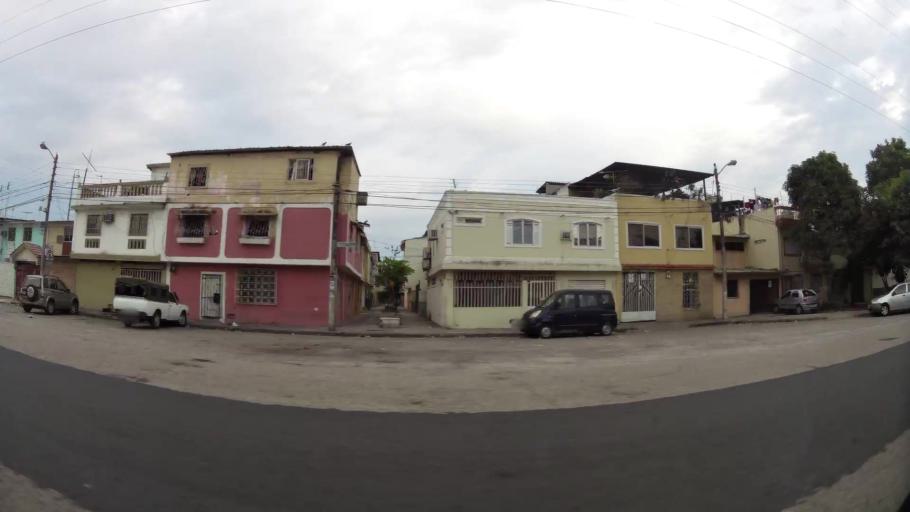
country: EC
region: Guayas
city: Guayaquil
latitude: -2.2367
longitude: -79.8883
